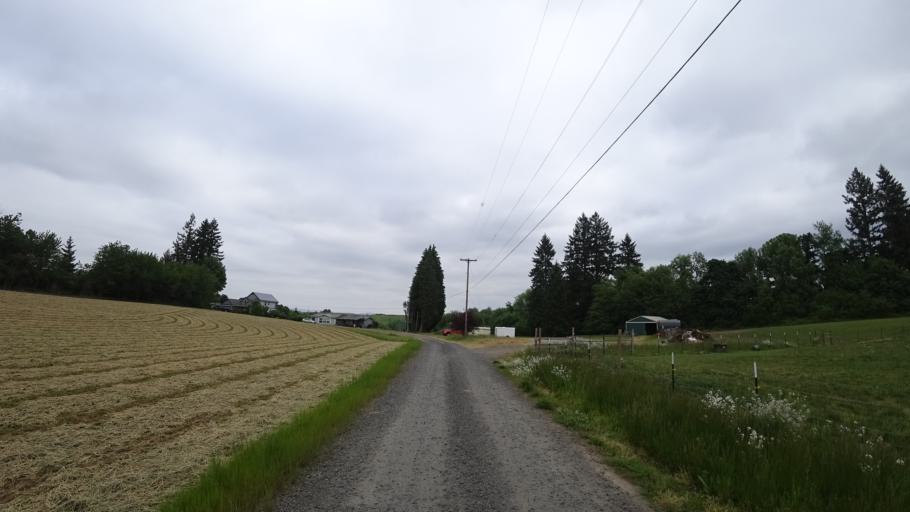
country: US
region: Oregon
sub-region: Washington County
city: Hillsboro
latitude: 45.4946
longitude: -122.9877
